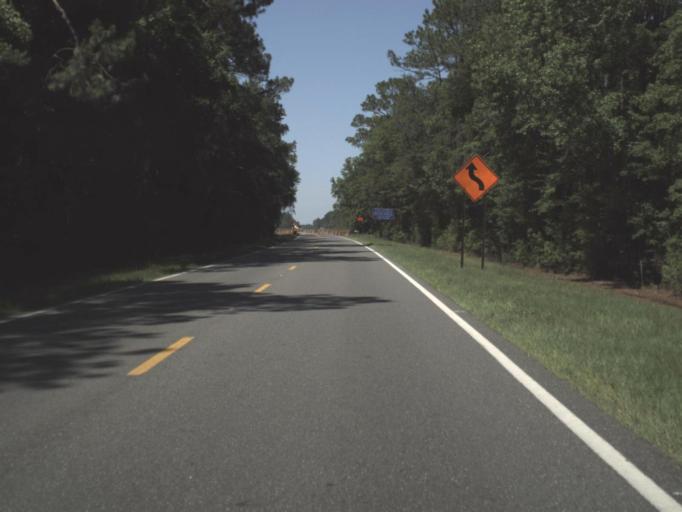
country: US
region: Florida
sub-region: Duval County
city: Baldwin
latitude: 30.3304
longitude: -81.9586
